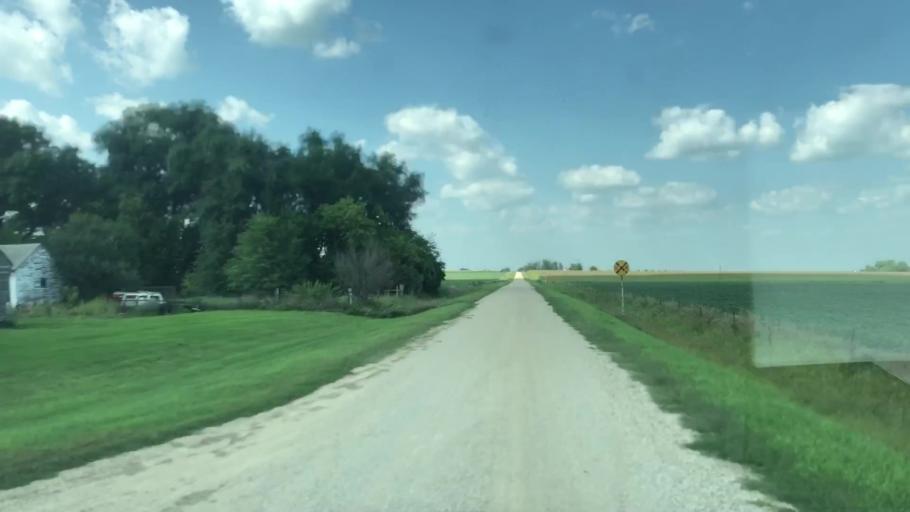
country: US
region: Iowa
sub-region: O'Brien County
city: Sheldon
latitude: 43.1760
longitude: -95.7824
